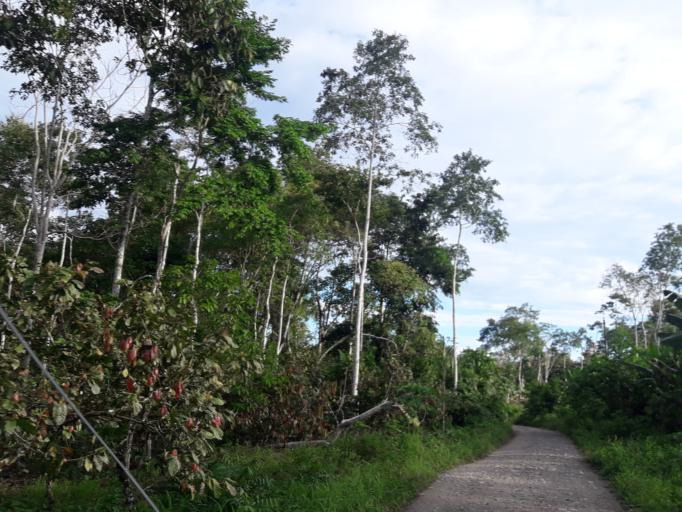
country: EC
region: Orellana
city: Boca Suno
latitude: -0.8965
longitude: -77.3089
